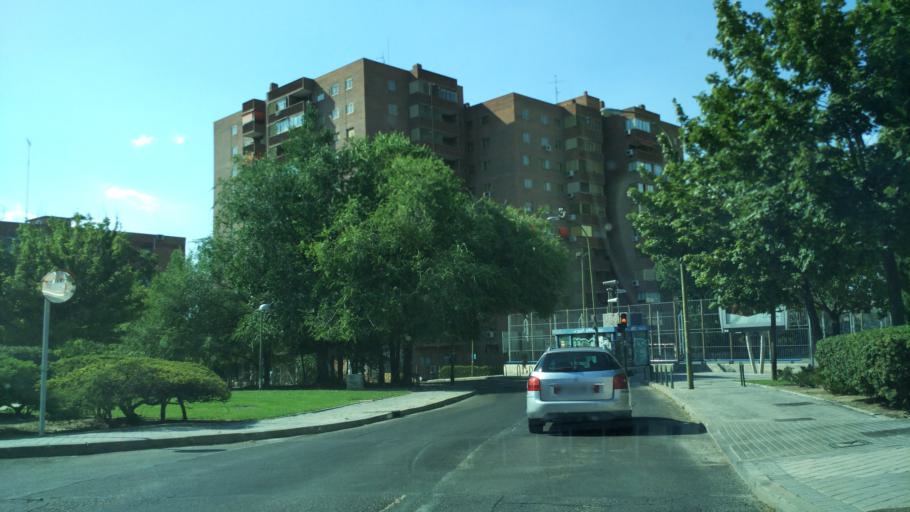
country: ES
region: Madrid
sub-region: Provincia de Madrid
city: Tetuan de las Victorias
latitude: 40.4634
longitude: -3.7209
